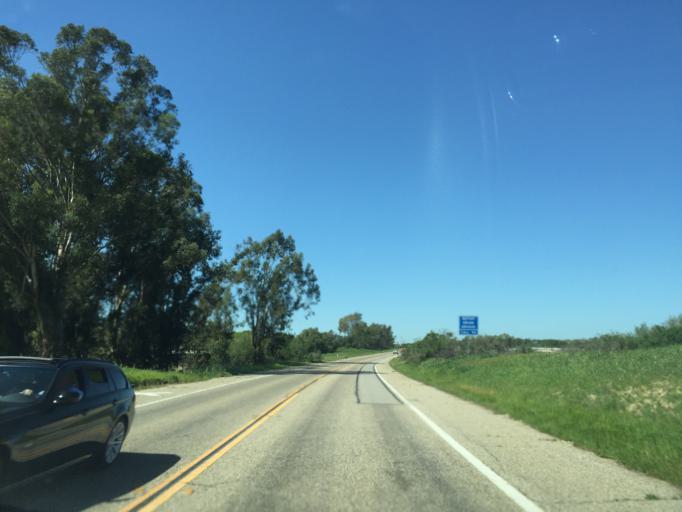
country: US
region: California
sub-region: Santa Barbara County
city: Santa Ynez
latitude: 34.6282
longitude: -120.0760
